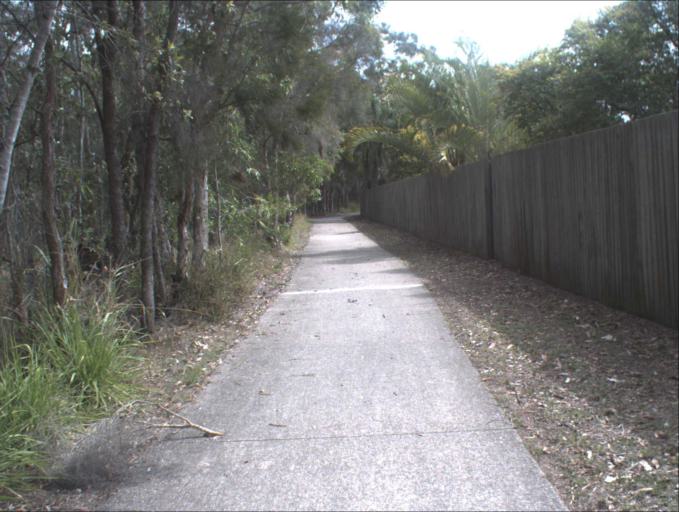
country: AU
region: Queensland
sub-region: Logan
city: Logan Reserve
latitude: -27.6884
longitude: 153.0610
